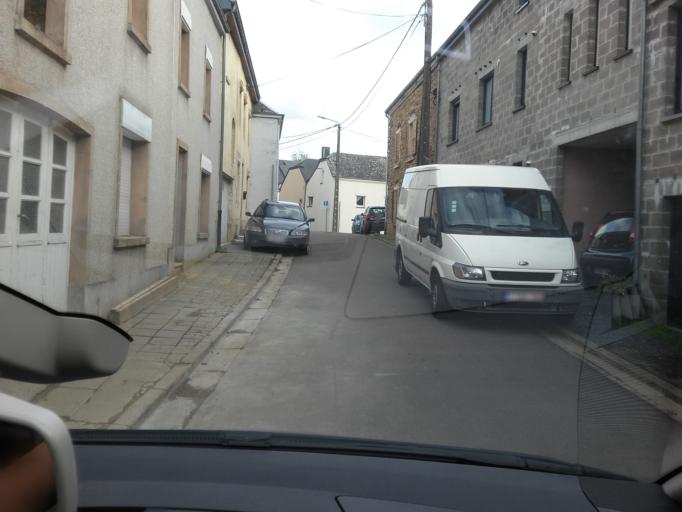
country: BE
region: Wallonia
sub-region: Province du Luxembourg
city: Arlon
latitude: 49.6978
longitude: 5.7650
